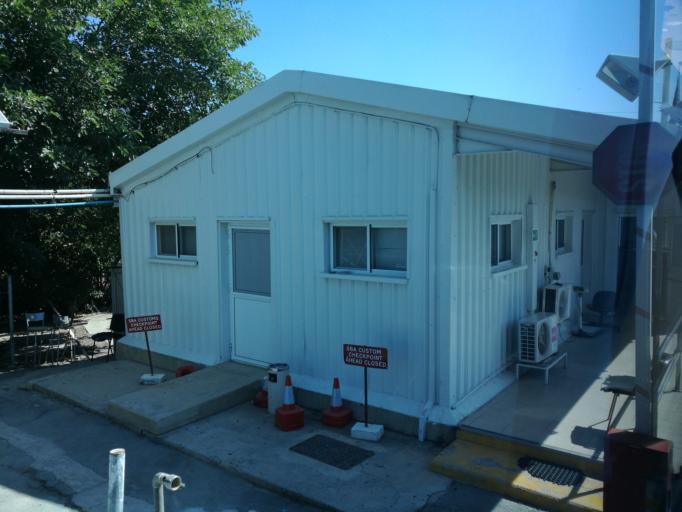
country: CY
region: Ammochostos
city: Acheritou
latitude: 35.0959
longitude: 33.9005
